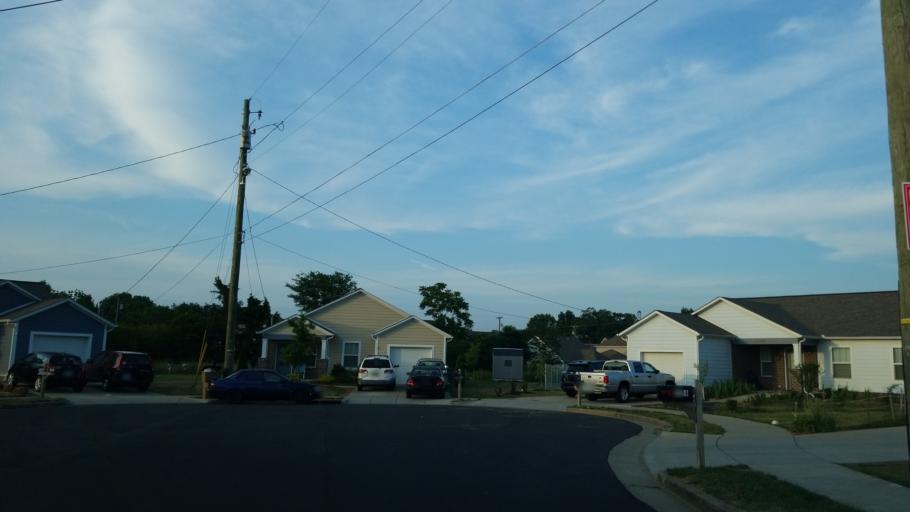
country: US
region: Tennessee
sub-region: Rutherford County
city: La Vergne
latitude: 36.0523
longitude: -86.5929
